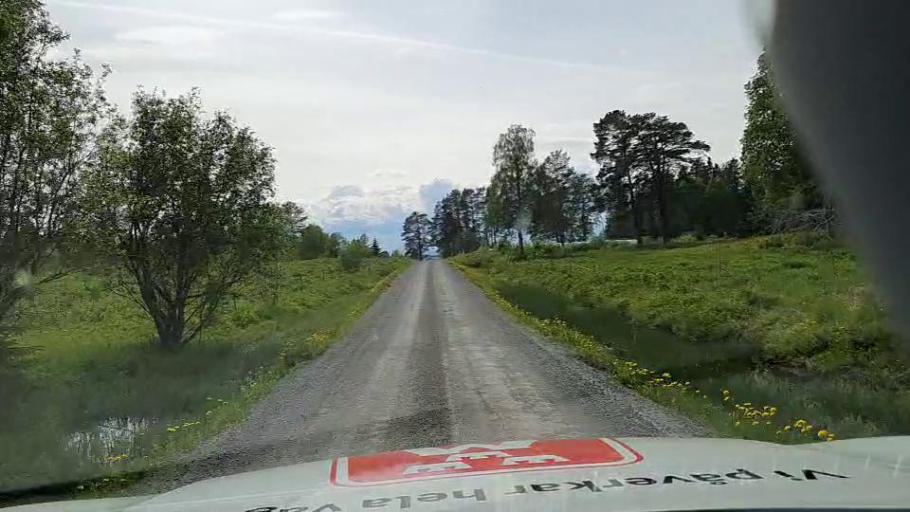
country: SE
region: Jaemtland
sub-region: OEstersunds Kommun
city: Brunflo
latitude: 62.9776
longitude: 14.6893
